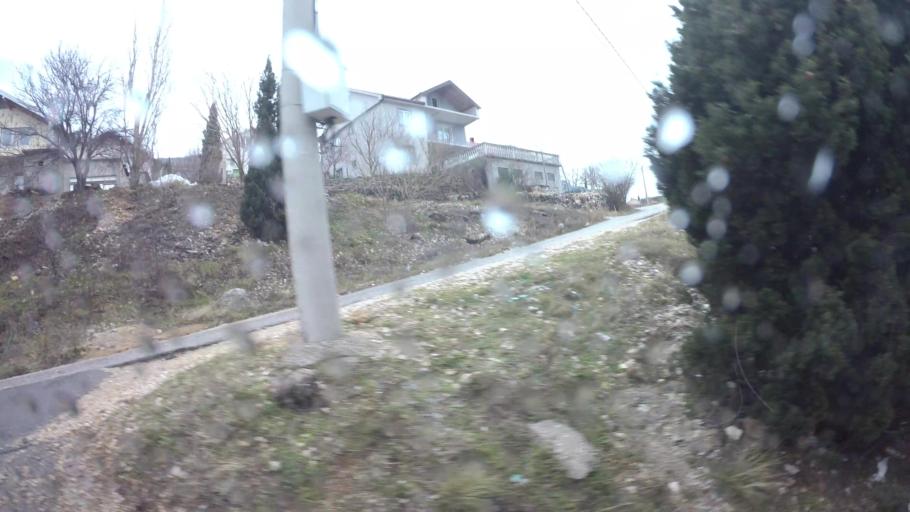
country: BA
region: Federation of Bosnia and Herzegovina
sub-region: Hercegovacko-Bosanski Kanton
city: Mostar
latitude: 43.3529
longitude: 17.8178
